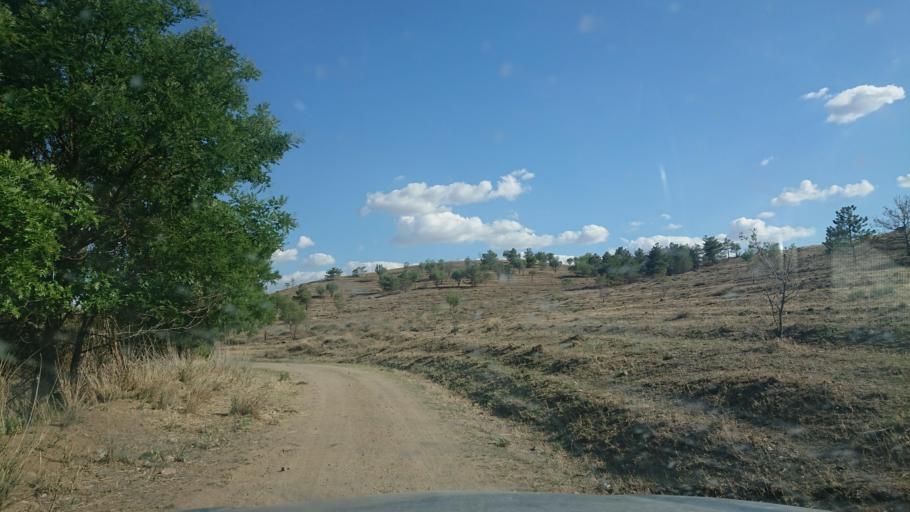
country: TR
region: Aksaray
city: Sariyahsi
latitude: 39.0225
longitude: 33.8953
